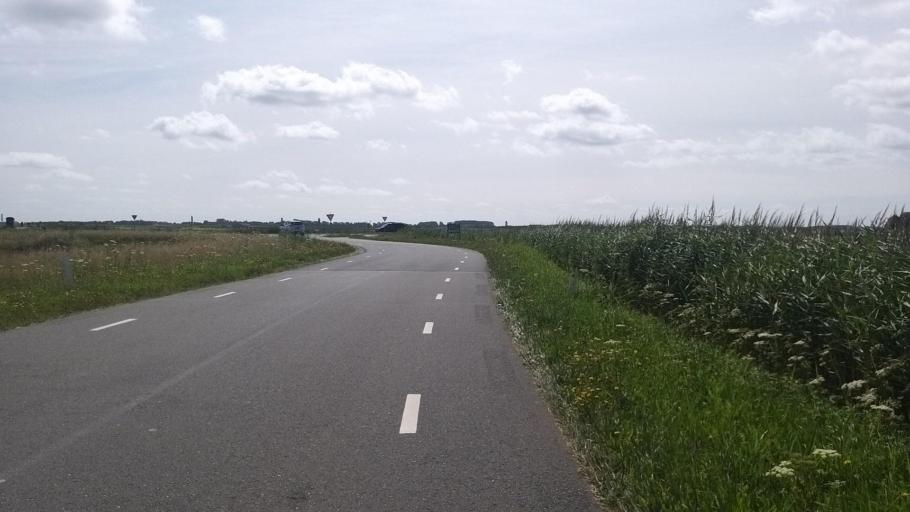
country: NL
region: North Holland
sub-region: Gemeente Texel
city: Den Burg
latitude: 53.0852
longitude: 4.7901
